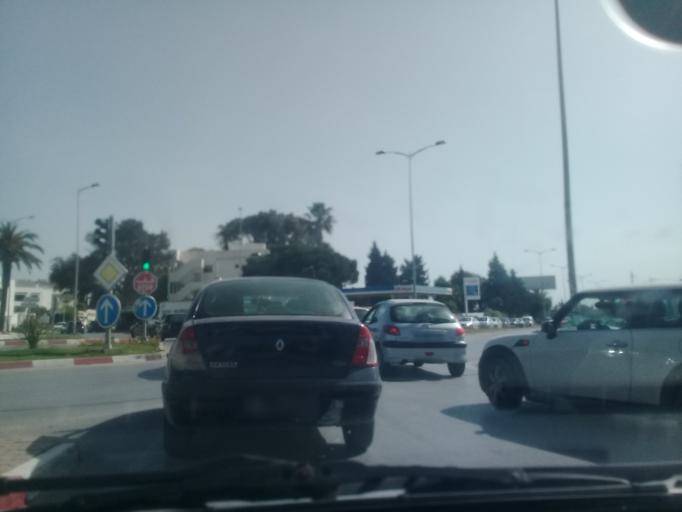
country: TN
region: Tunis
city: Al Marsa
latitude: 36.8768
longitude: 10.3264
